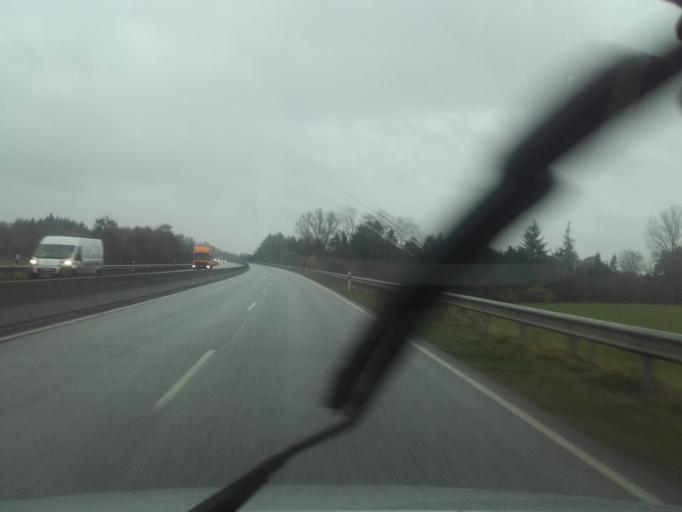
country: DE
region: Schleswig-Holstein
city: Westerronfeld
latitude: 54.3038
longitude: 9.6371
